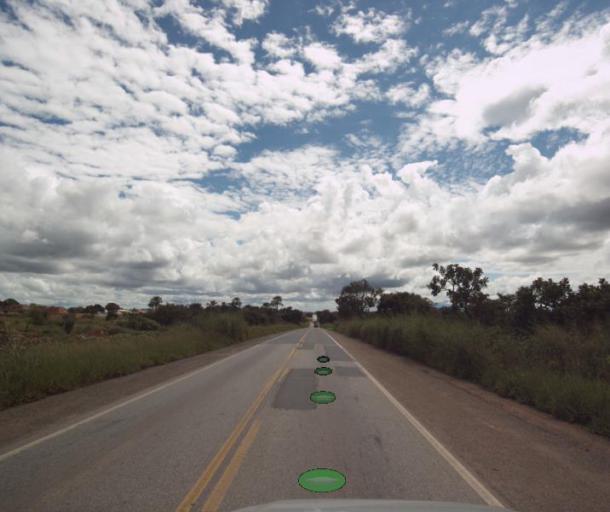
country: BR
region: Goias
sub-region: Uruacu
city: Uruacu
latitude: -14.3252
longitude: -49.1524
